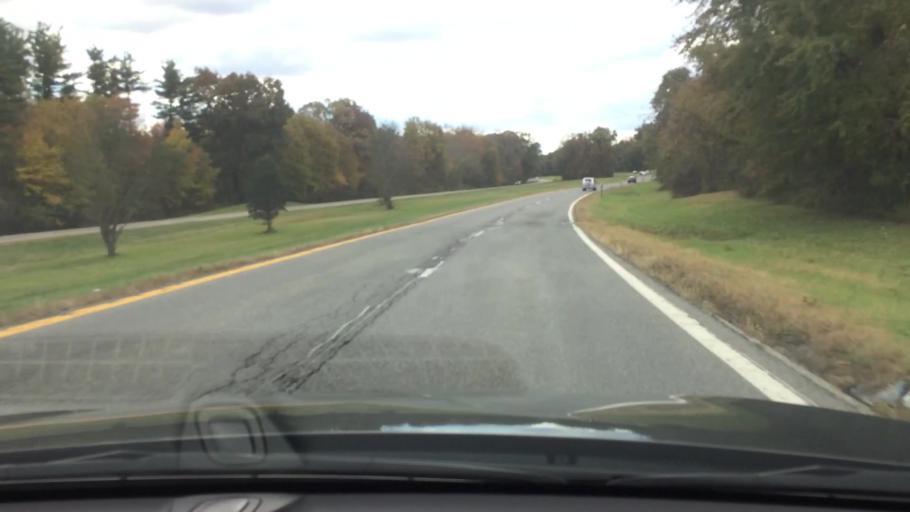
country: US
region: New York
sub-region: Dutchess County
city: Hillside Lake
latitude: 41.6085
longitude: -73.7610
